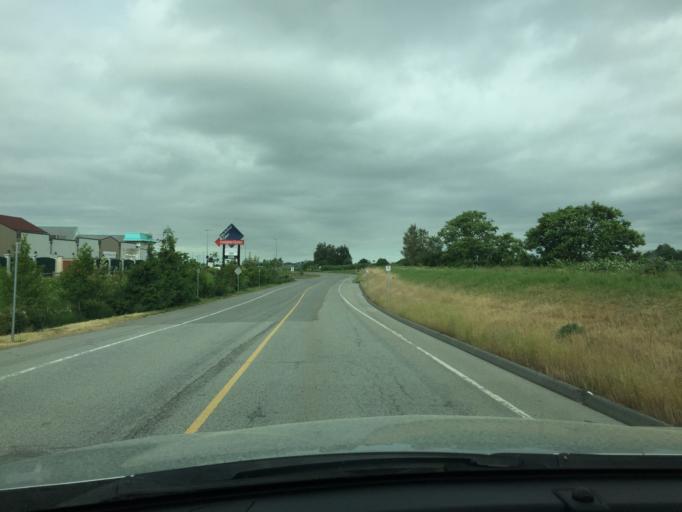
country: CA
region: British Columbia
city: Richmond
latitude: 49.1986
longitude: -123.1393
